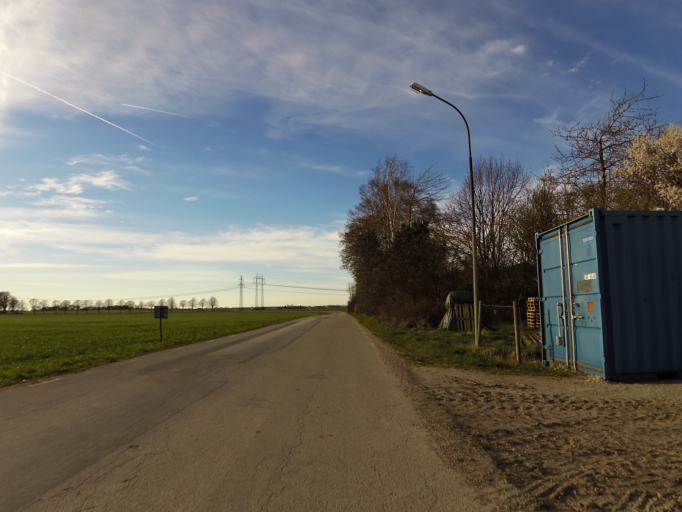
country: SE
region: Skane
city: Bjarred
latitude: 55.7402
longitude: 13.0610
